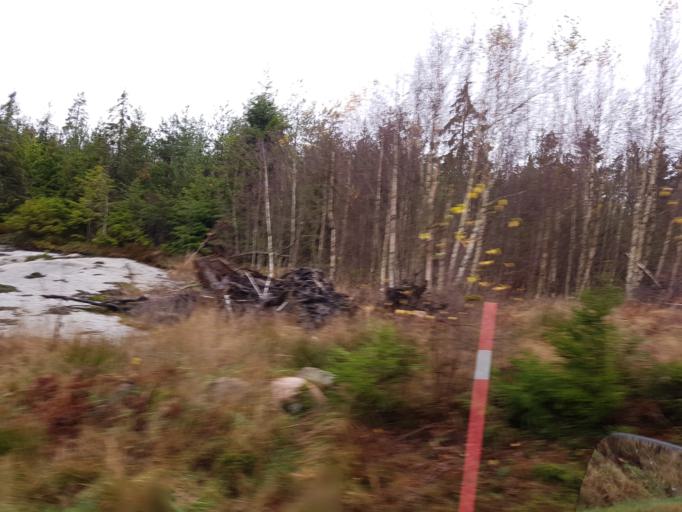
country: SE
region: Vaestra Goetaland
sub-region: Orust
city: Henan
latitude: 58.2229
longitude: 11.7702
